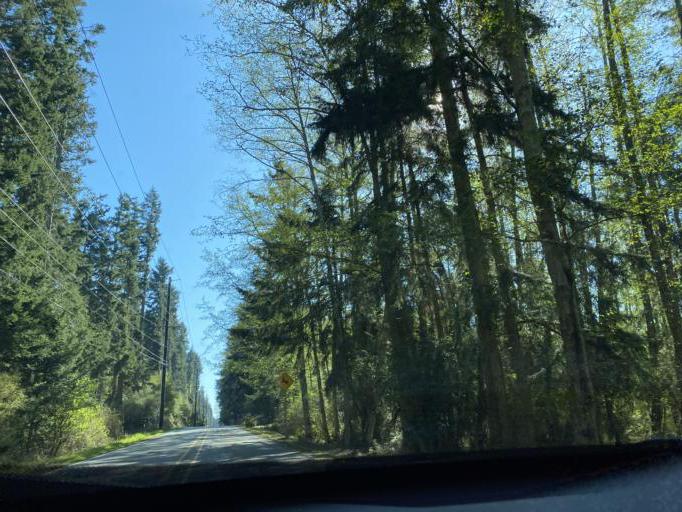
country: US
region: Washington
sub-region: Island County
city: Freeland
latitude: 48.0797
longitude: -122.6021
